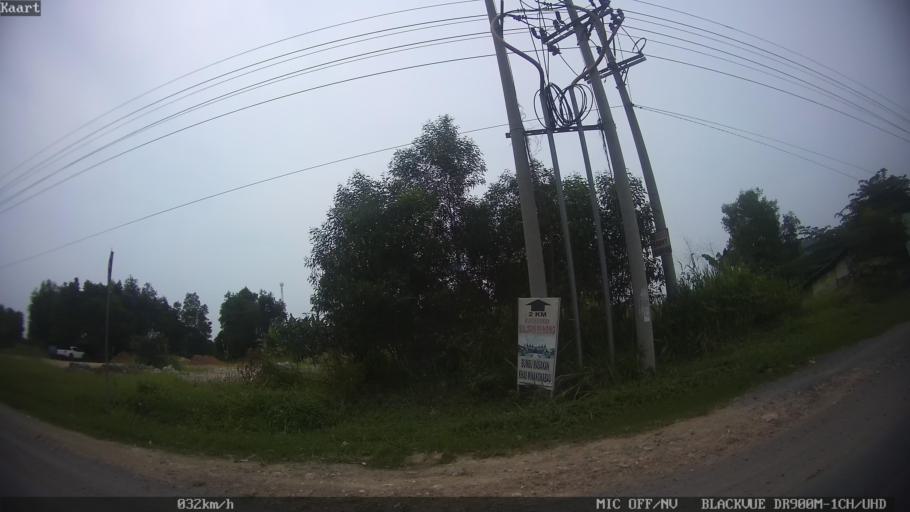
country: ID
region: Lampung
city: Panjang
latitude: -5.4152
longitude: 105.3449
